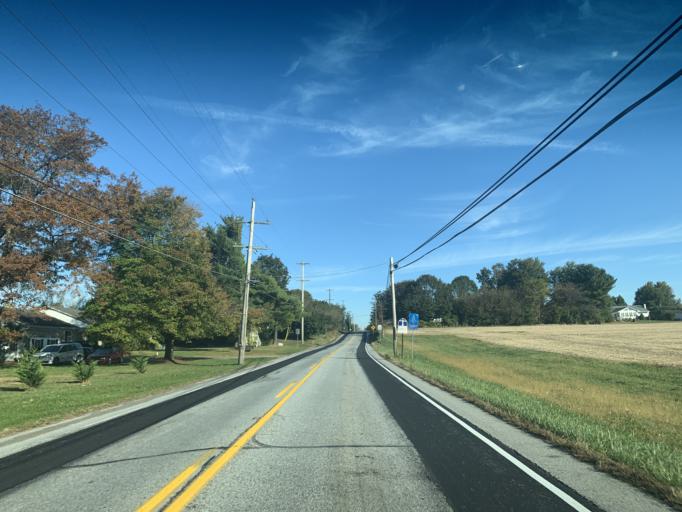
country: US
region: Pennsylvania
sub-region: Chester County
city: Parkesburg
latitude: 39.8858
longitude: -75.9226
